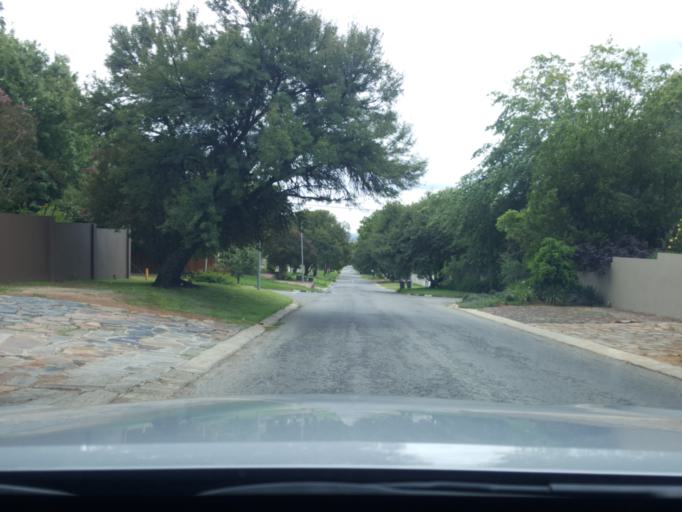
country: ZA
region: Gauteng
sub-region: City of Johannesburg Metropolitan Municipality
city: Johannesburg
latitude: -26.1124
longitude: 28.0048
